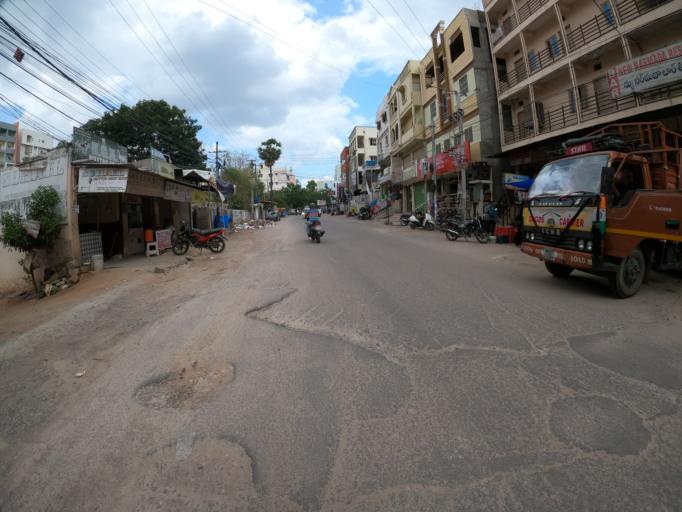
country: IN
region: Telangana
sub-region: Hyderabad
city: Hyderabad
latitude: 17.4072
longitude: 78.3890
